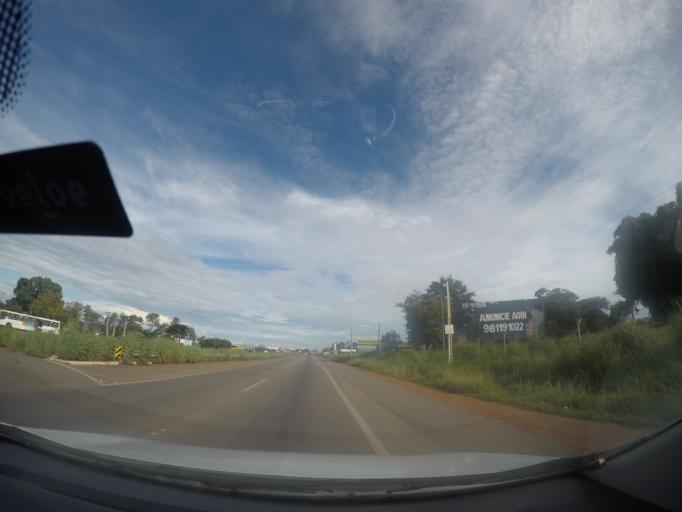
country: BR
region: Goias
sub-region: Goiania
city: Goiania
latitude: -16.6211
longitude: -49.3568
